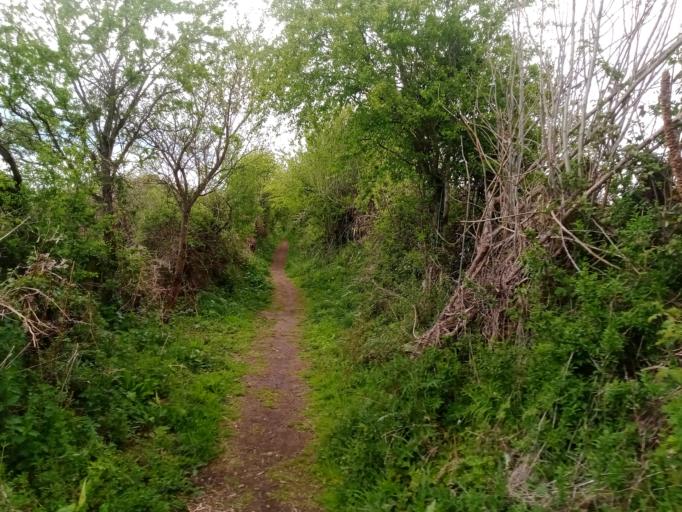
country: IE
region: Leinster
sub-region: Kilkenny
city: Kilkenny
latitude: 52.6922
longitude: -7.2656
